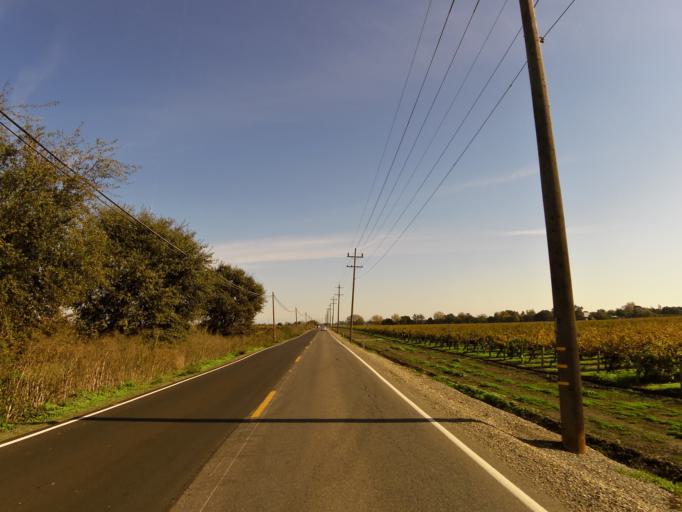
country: US
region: California
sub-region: Sacramento County
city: Walnut Grove
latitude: 38.2768
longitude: -121.4926
